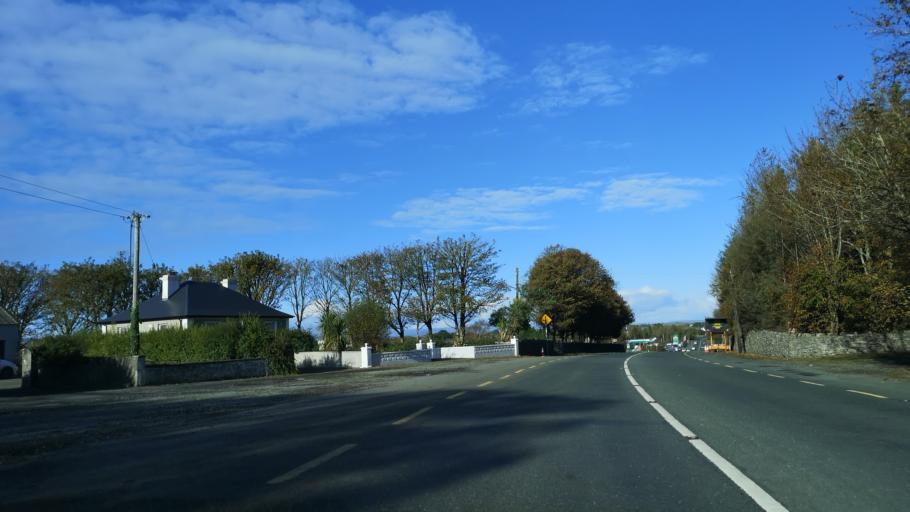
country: IE
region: Connaught
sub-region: County Galway
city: Moycullen
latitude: 53.4479
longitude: -9.0888
